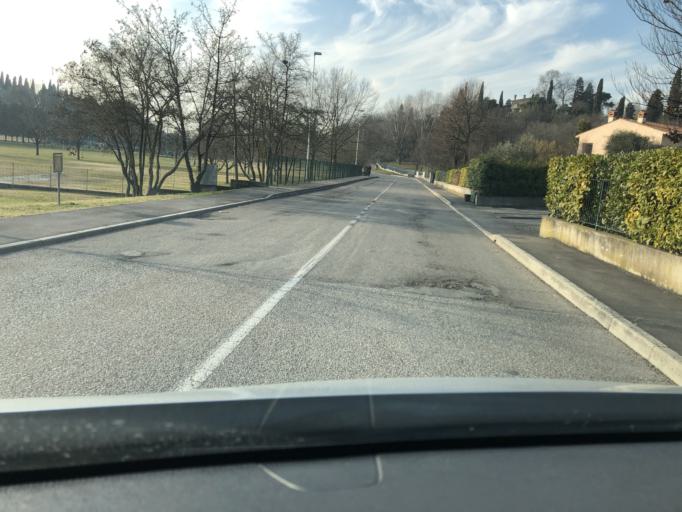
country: IT
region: Veneto
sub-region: Provincia di Verona
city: Sommacampagna
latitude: 45.4110
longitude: 10.8461
